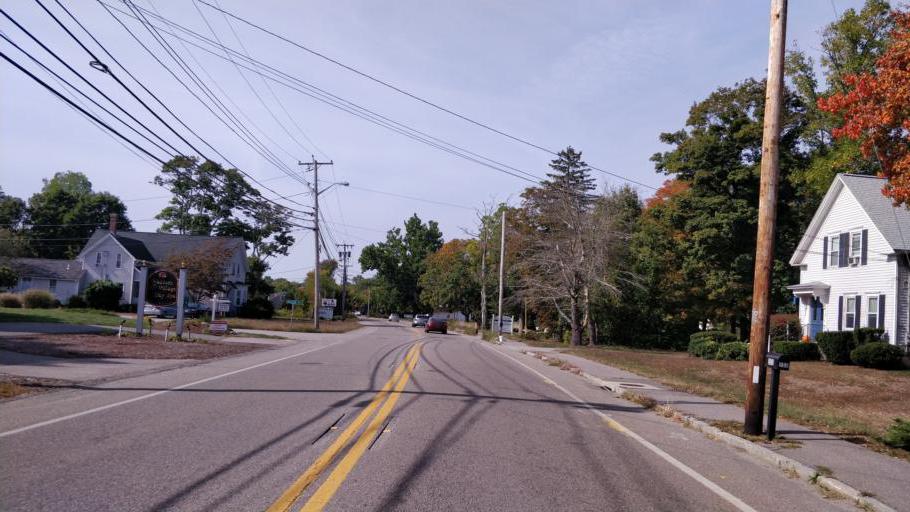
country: US
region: Massachusetts
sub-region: Bristol County
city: Norton
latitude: 41.9598
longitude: -71.2046
